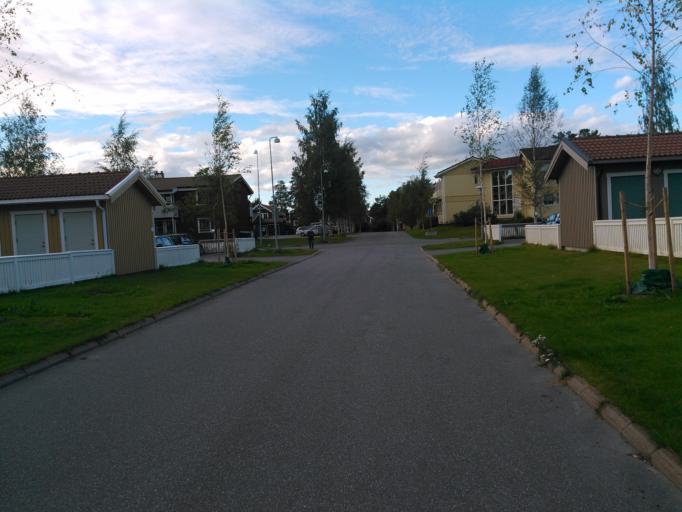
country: SE
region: Vaesterbotten
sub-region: Umea Kommun
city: Ersmark
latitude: 63.8073
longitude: 20.3381
